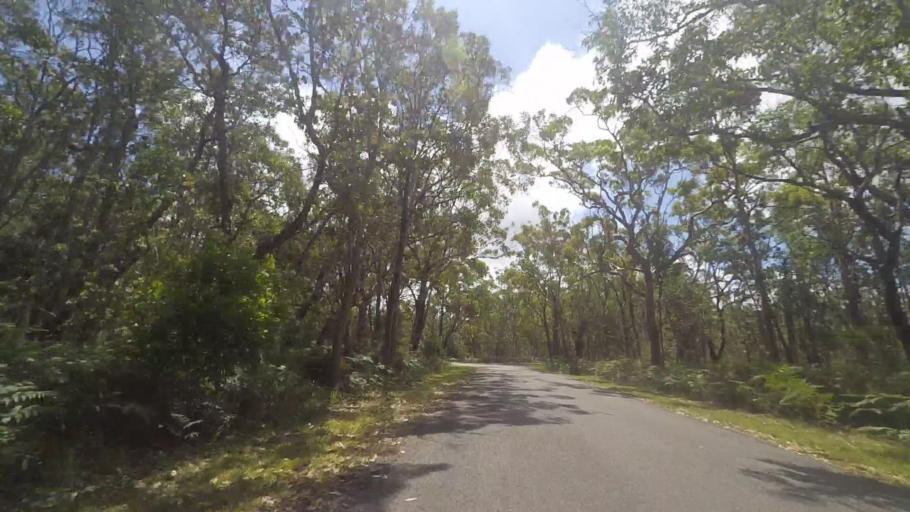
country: AU
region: New South Wales
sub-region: Great Lakes
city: Bulahdelah
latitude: -32.5032
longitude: 152.3091
